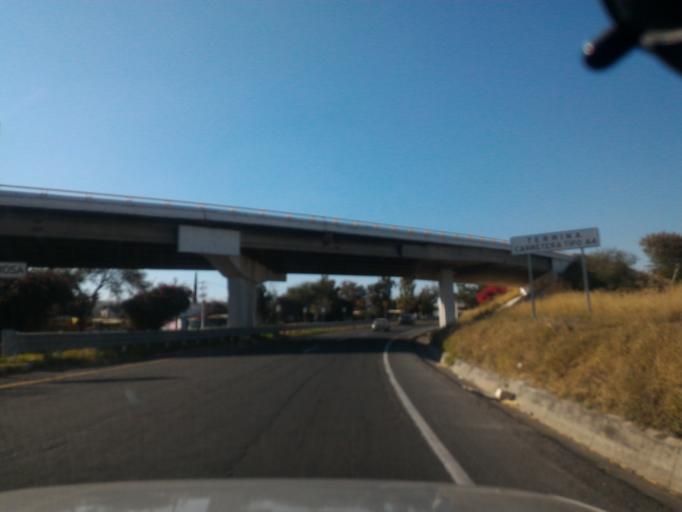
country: MX
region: Jalisco
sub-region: Ixtlahuacan de los Membrillos
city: Los Olivos
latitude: 20.4150
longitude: -103.2329
